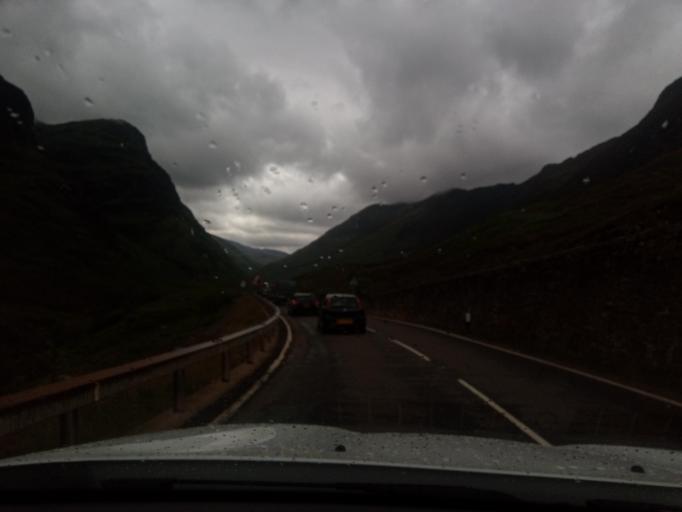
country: GB
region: Scotland
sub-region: Highland
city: Fort William
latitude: 56.6649
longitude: -4.9717
